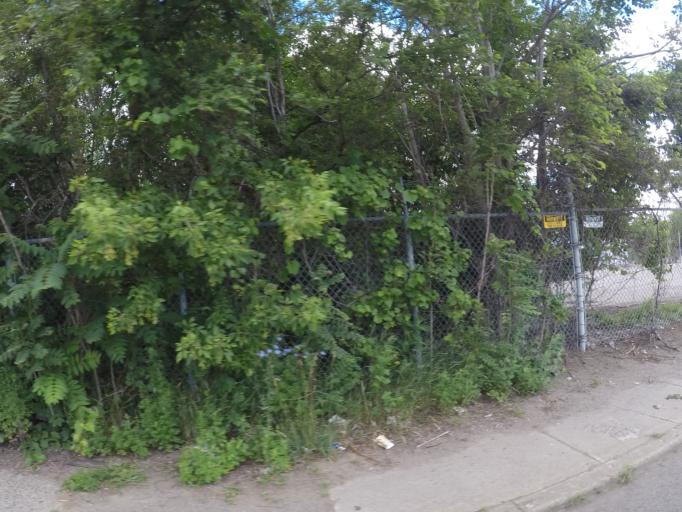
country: US
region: Michigan
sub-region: Wayne County
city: Hamtramck
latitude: 42.4195
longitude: -83.0281
